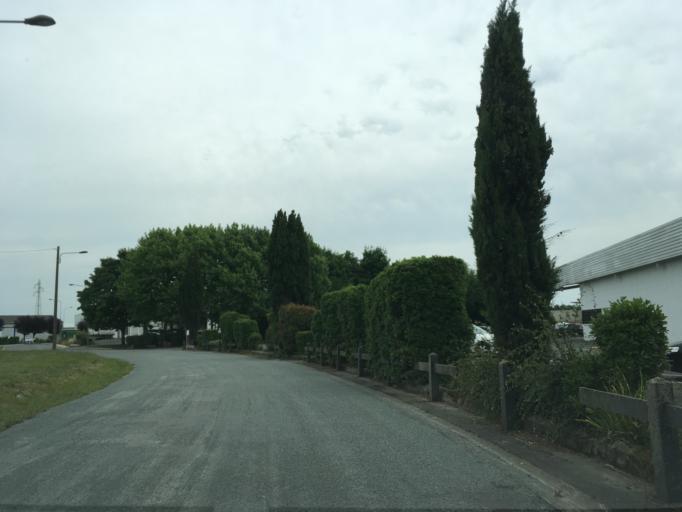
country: FR
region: Poitou-Charentes
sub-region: Departement des Deux-Sevres
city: Bessines
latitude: 46.3108
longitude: -0.4931
